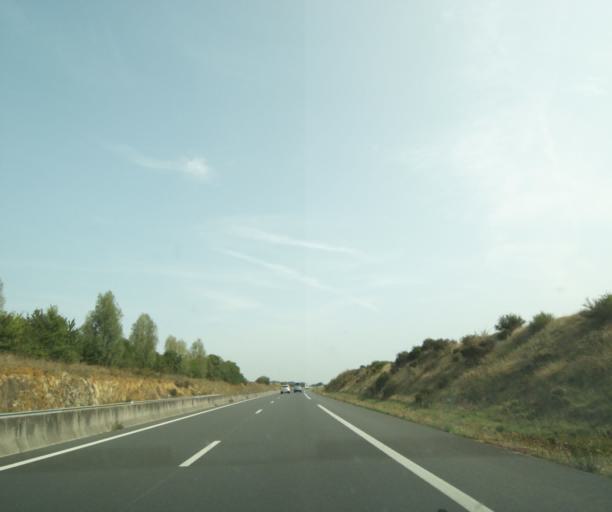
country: FR
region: Pays de la Loire
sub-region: Departement de la Sarthe
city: Arconnay
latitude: 48.3590
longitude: 0.0972
